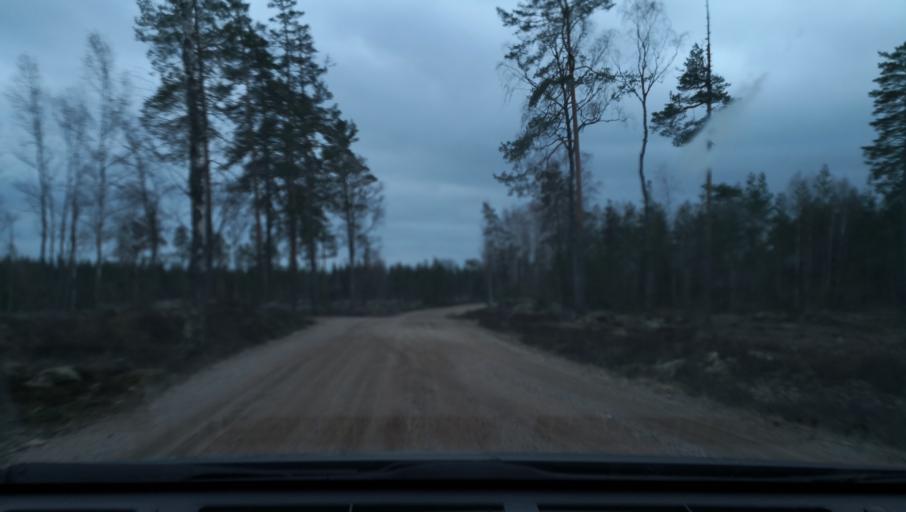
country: SE
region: OErebro
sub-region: Lindesbergs Kommun
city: Fellingsbro
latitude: 59.5937
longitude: 15.5775
